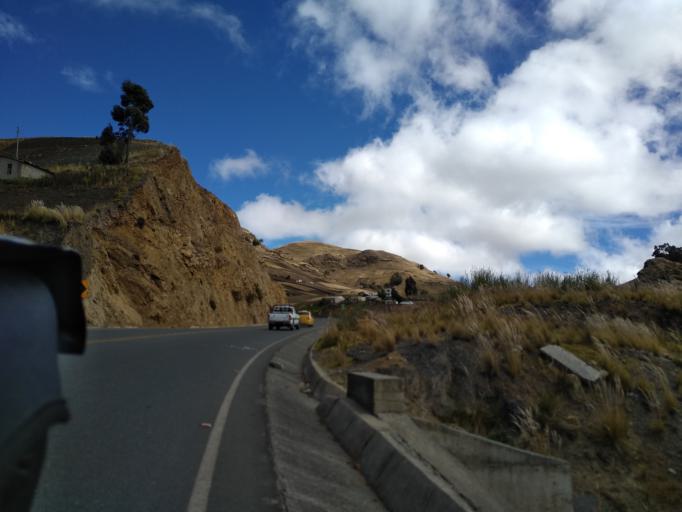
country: EC
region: Cotopaxi
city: Pujili
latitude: -0.9627
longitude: -78.9078
